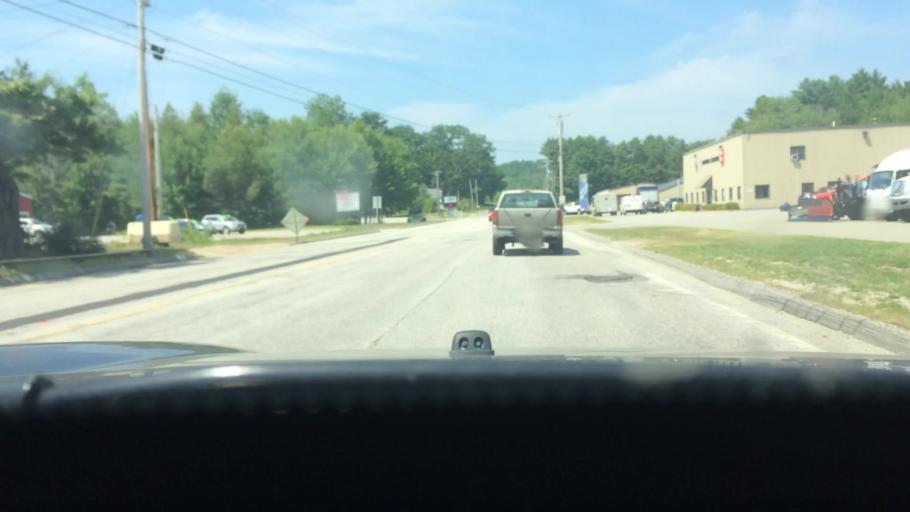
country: US
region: Maine
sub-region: Androscoggin County
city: Minot
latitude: 44.0807
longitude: -70.2788
